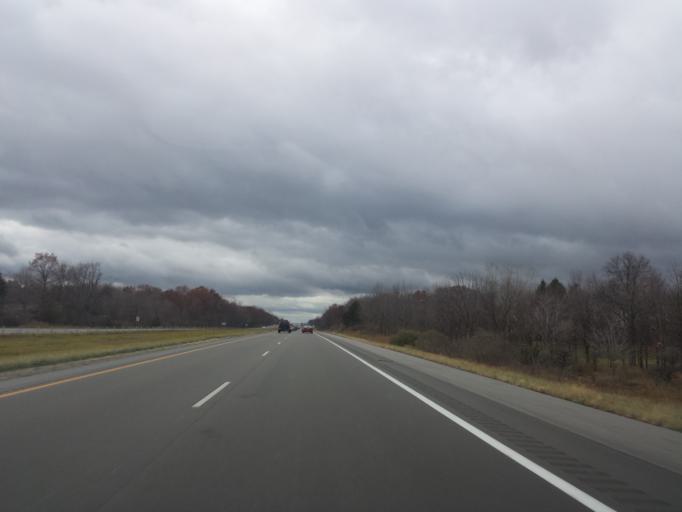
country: US
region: Michigan
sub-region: Genesee County
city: Swartz Creek
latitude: 42.9649
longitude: -83.8686
